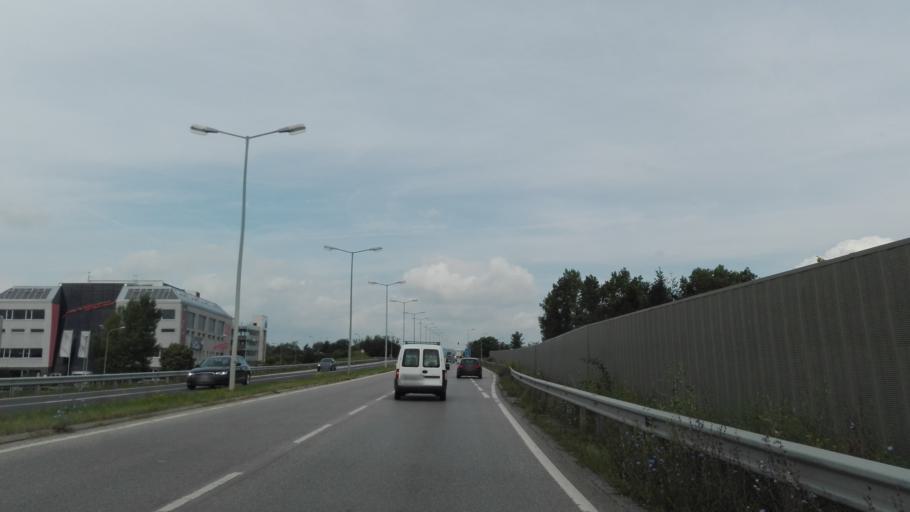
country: AT
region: Lower Austria
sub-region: Politischer Bezirk Modling
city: Brunn am Gebirge
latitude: 48.1142
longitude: 16.3021
